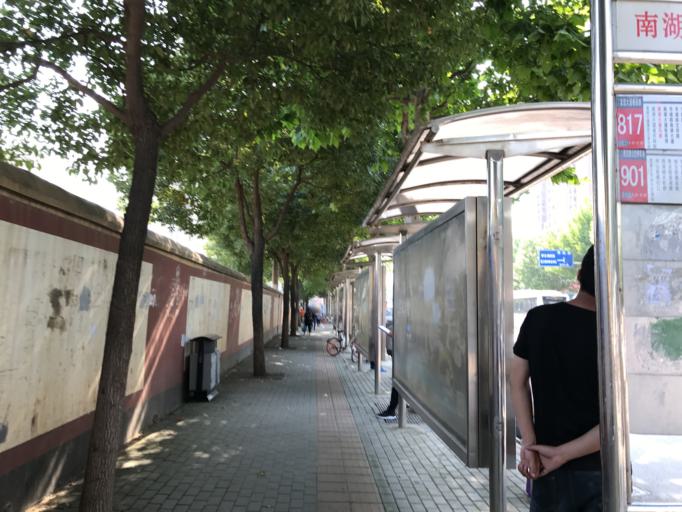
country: CN
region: Hubei
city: Shizishan
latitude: 30.4840
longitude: 114.3220
